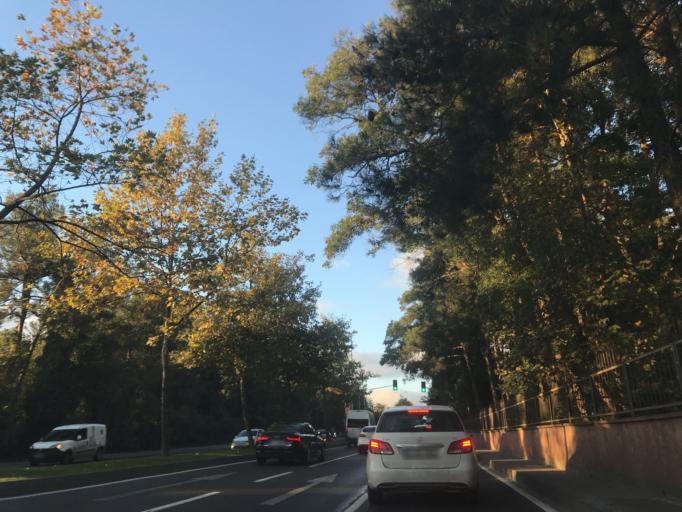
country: TR
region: Istanbul
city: Sisli
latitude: 41.1293
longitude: 29.0243
